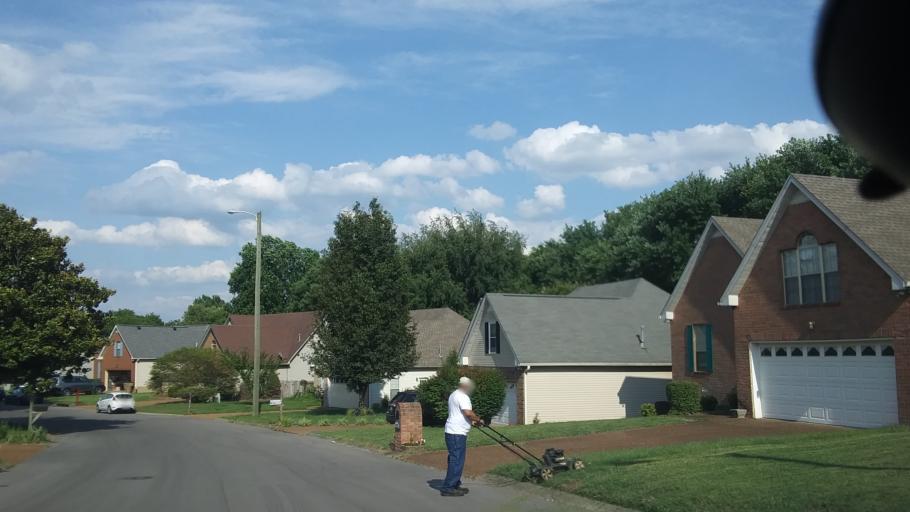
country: US
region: Tennessee
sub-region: Rutherford County
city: La Vergne
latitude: 36.0868
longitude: -86.6580
